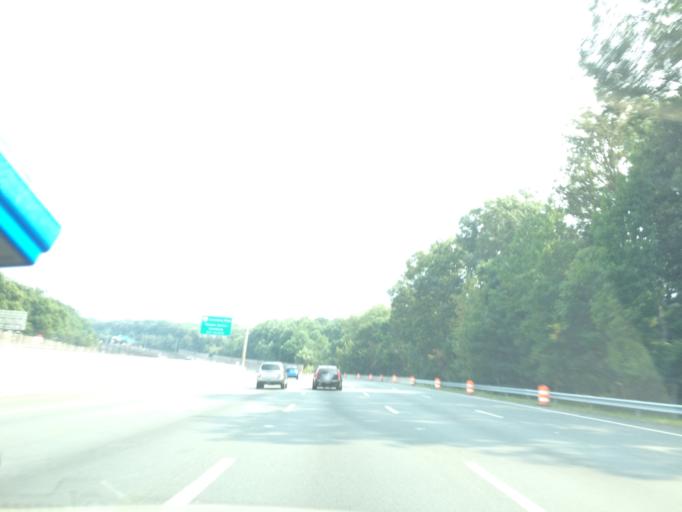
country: US
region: Virginia
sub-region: Fairfax County
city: Wolf Trap
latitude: 38.9340
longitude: -77.2649
